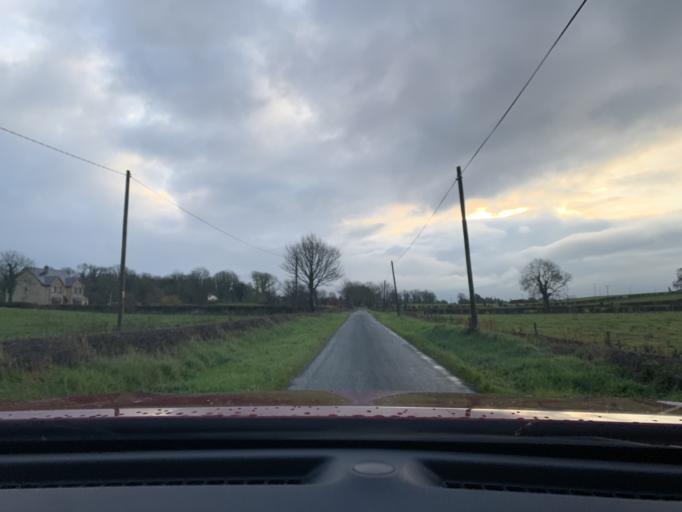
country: IE
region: Connaught
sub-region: Sligo
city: Ballymote
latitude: 54.0378
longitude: -8.5477
